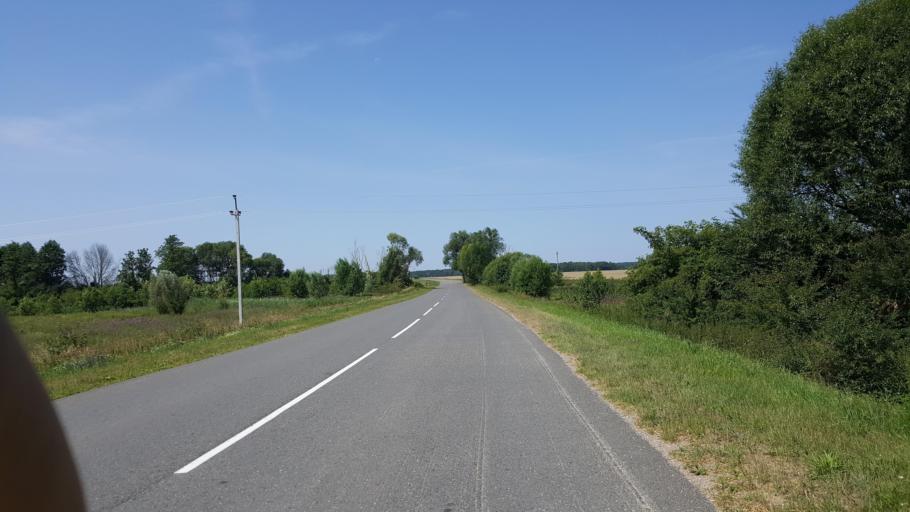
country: BY
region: Brest
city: Kamyanyets
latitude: 52.3806
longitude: 23.6551
